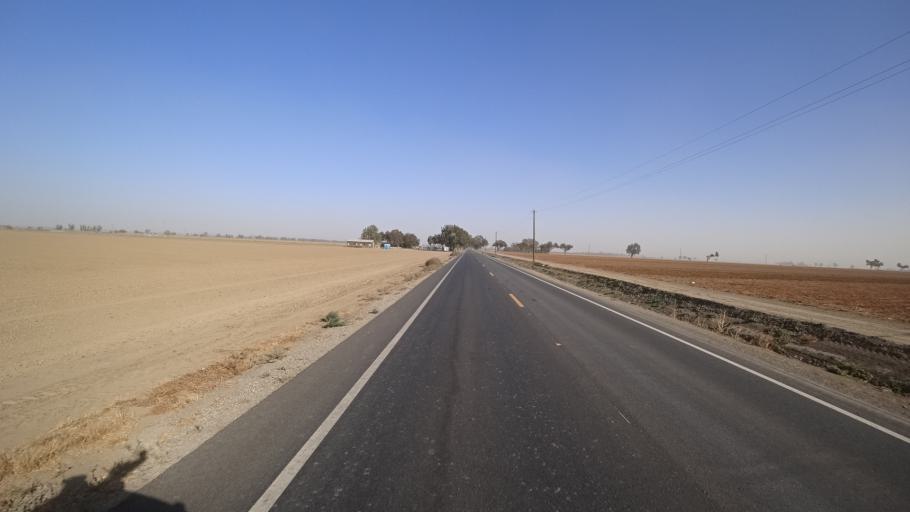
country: US
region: California
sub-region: Yolo County
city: Woodland
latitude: 38.7931
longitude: -121.7698
